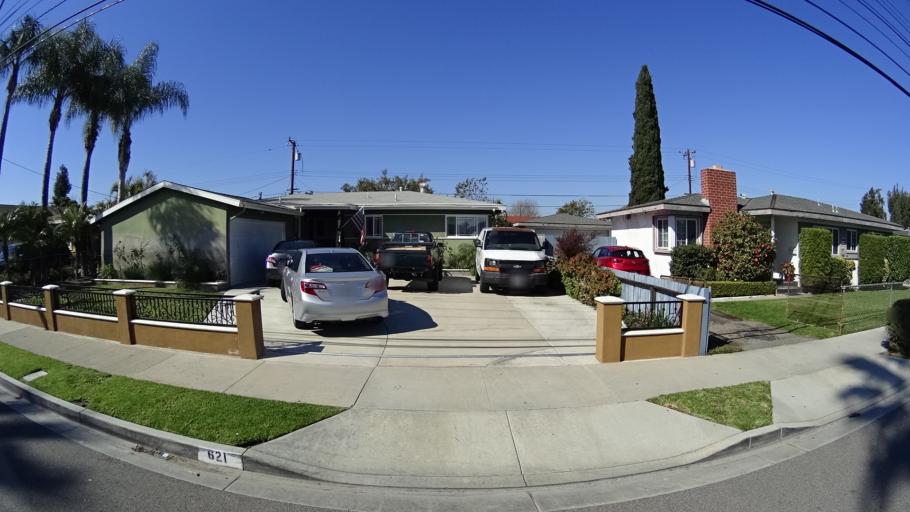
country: US
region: California
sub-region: Orange County
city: Anaheim
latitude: 33.8247
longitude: -117.9285
